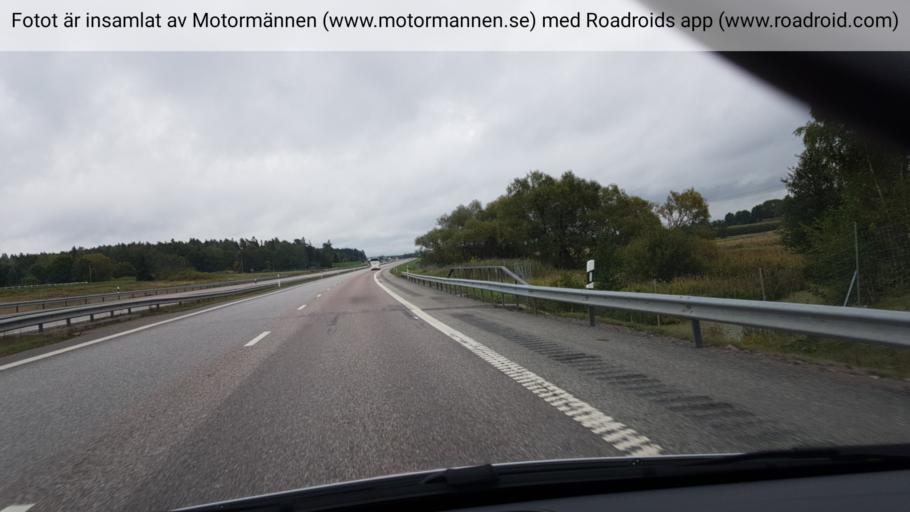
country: SE
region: Soedermanland
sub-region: Strangnas Kommun
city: Strangnas
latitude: 59.3645
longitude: 16.8702
